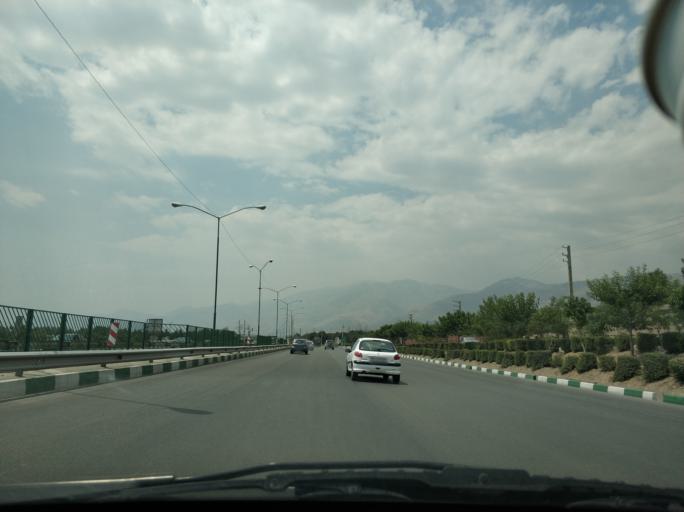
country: IR
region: Tehran
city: Tajrish
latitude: 35.7675
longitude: 51.5617
